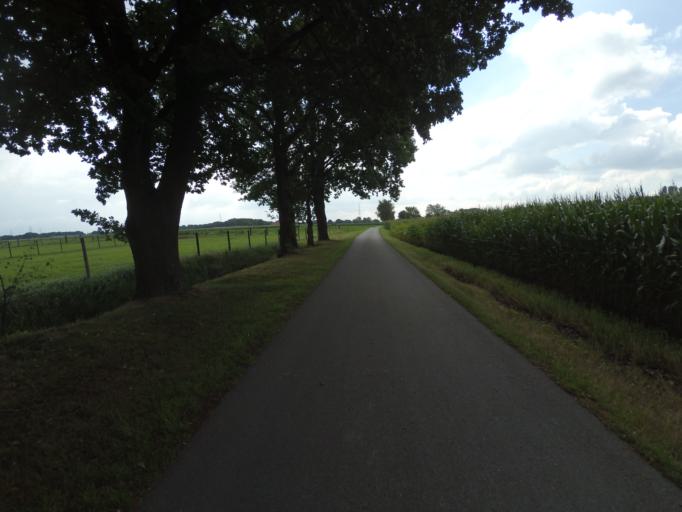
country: BE
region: Flanders
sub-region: Provincie Limburg
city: Kinrooi
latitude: 51.1178
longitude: 5.7490
